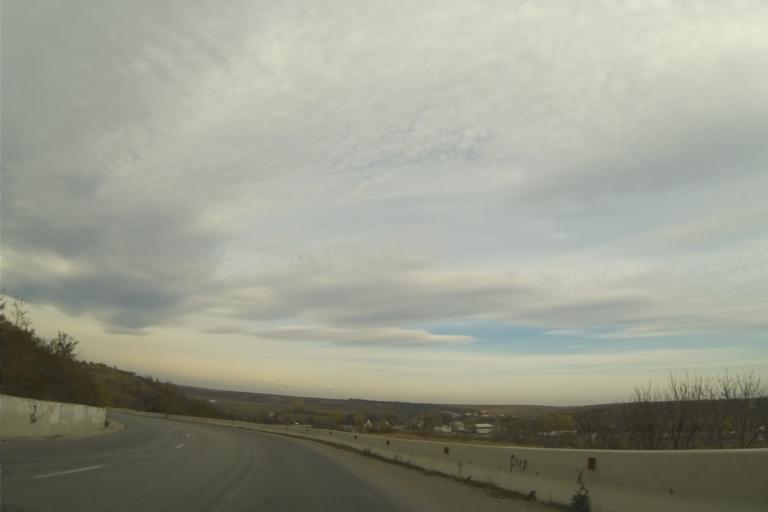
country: RO
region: Olt
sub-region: Comuna Valea Mare
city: Valea Mare
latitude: 44.4771
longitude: 24.4342
